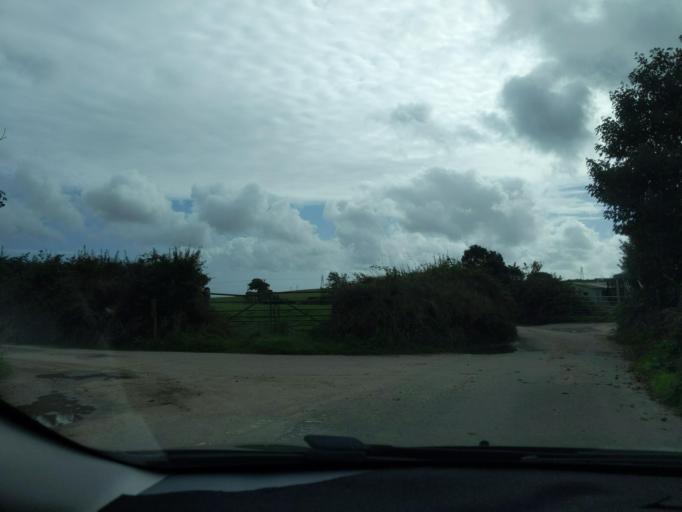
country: GB
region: England
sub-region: Cornwall
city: Lostwithiel
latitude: 50.3915
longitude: -4.7041
